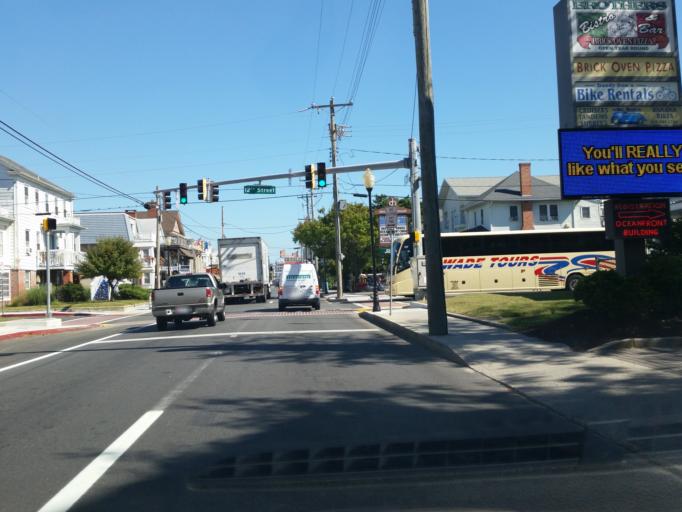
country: US
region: Maryland
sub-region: Worcester County
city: Ocean City
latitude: 38.3418
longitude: -75.0806
